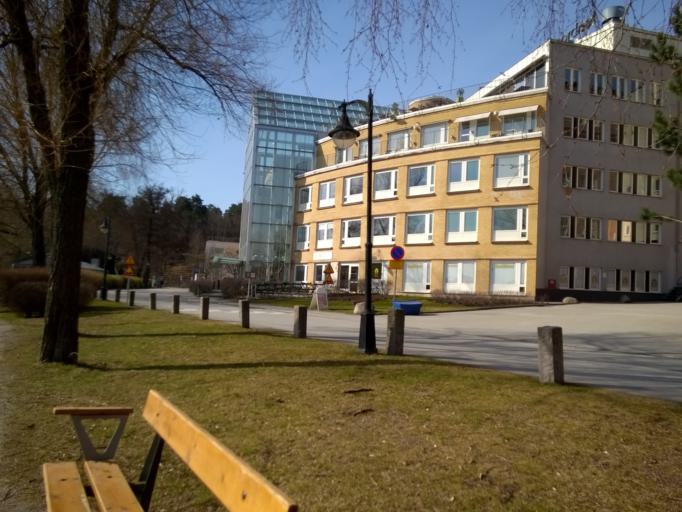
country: SE
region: Stockholm
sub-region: Solna Kommun
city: Solna
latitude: 59.3289
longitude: 17.9855
